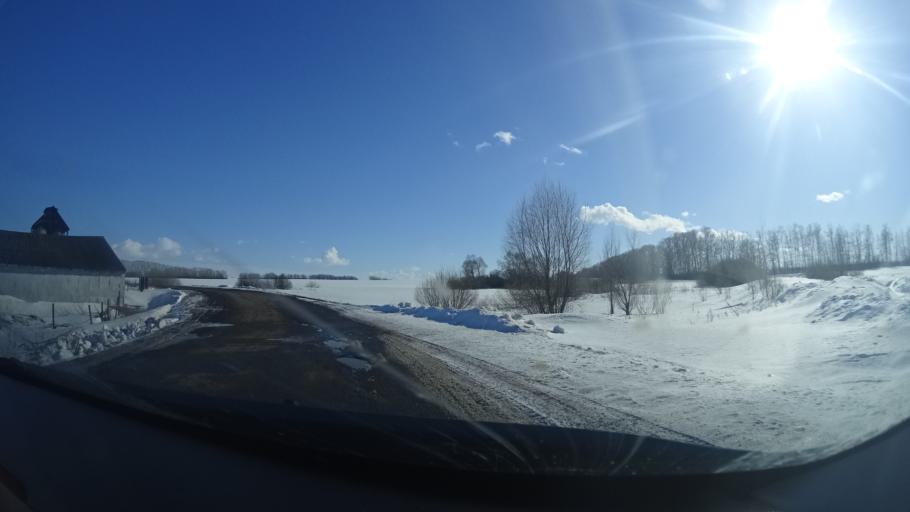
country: RU
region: Bashkortostan
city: Chishmy
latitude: 54.5895
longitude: 55.2572
